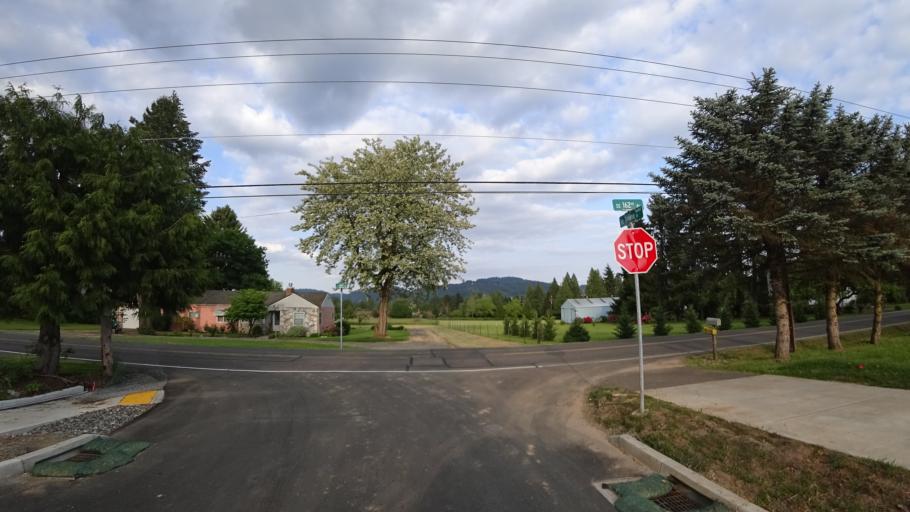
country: US
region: Oregon
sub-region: Clackamas County
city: Happy Valley
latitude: 45.4628
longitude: -122.4970
